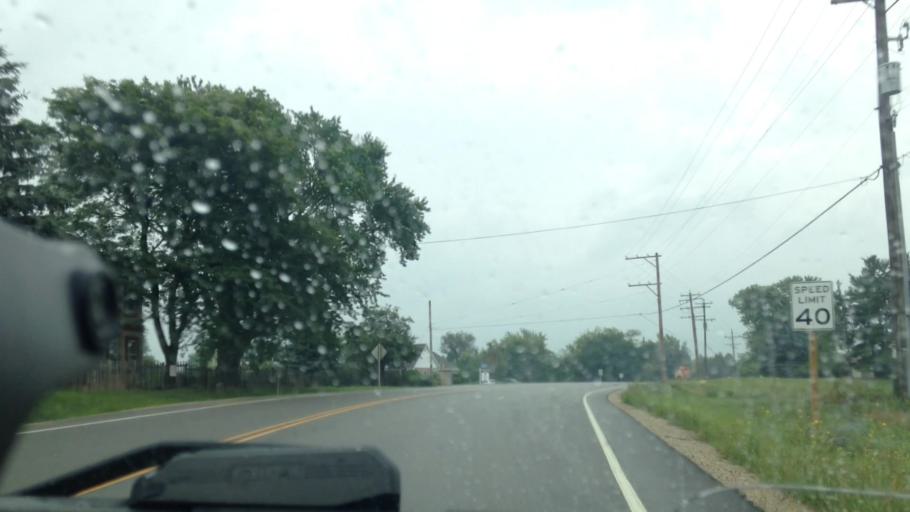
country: US
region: Wisconsin
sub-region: Washington County
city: Slinger
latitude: 43.3227
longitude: -88.2694
